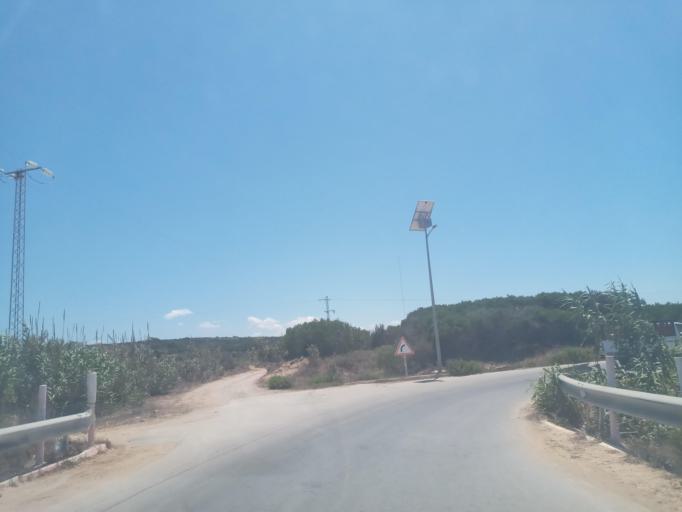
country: TN
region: Nabul
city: El Haouaria
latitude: 37.0492
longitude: 10.9803
